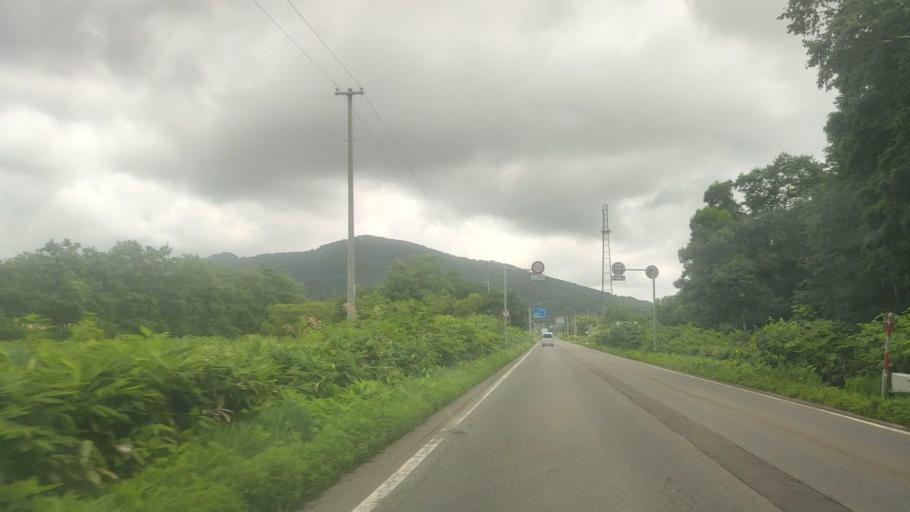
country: JP
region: Hokkaido
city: Niseko Town
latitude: 42.6021
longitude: 140.4838
